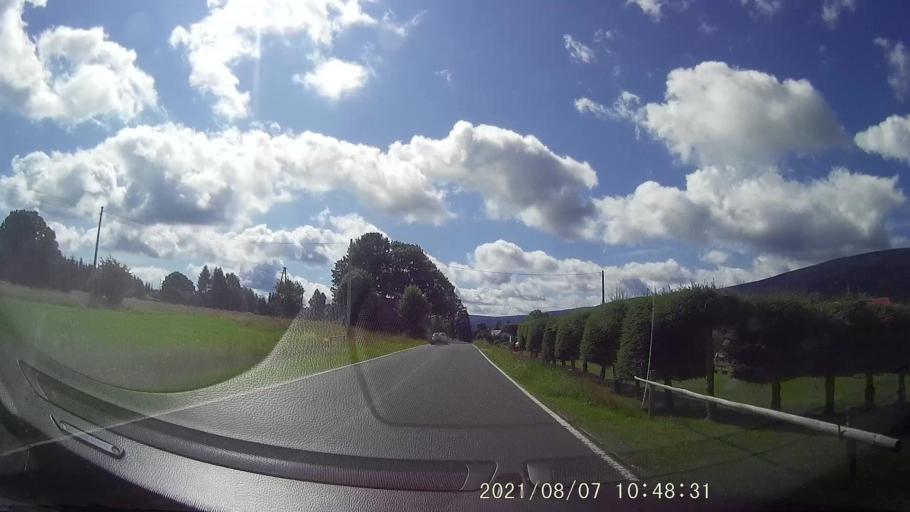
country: PL
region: Lower Silesian Voivodeship
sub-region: Powiat klodzki
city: Szczytna
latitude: 50.3100
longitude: 16.4497
